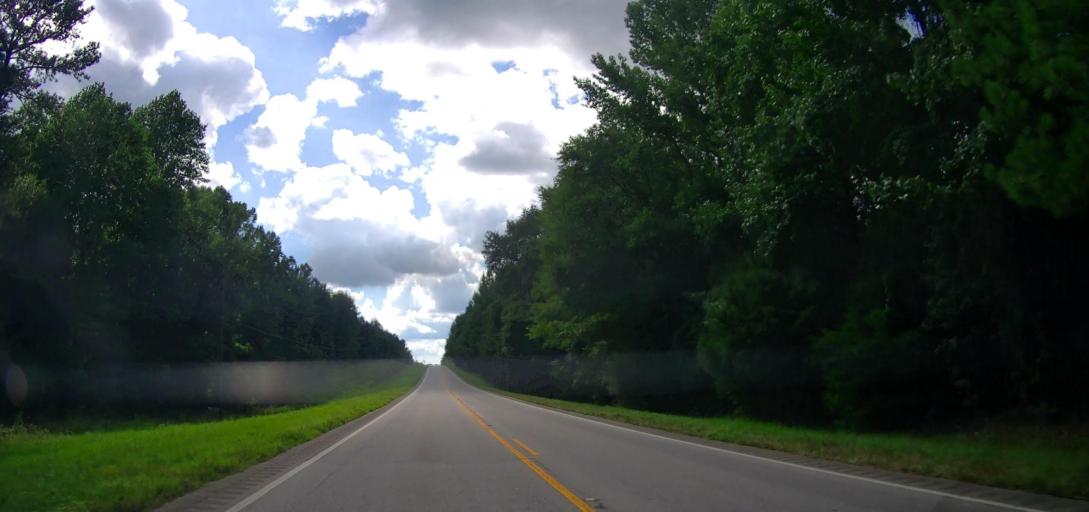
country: US
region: Alabama
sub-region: Lee County
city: Auburn
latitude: 32.4431
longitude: -85.4993
